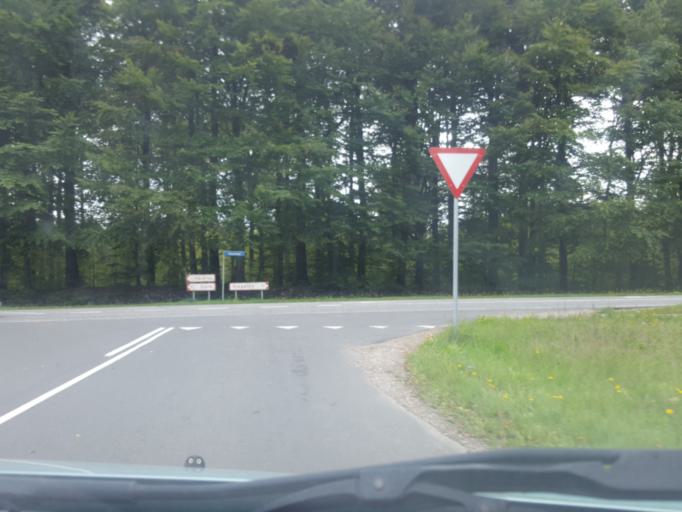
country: DK
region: Zealand
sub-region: Soro Kommune
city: Soro
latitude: 55.4419
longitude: 11.5264
